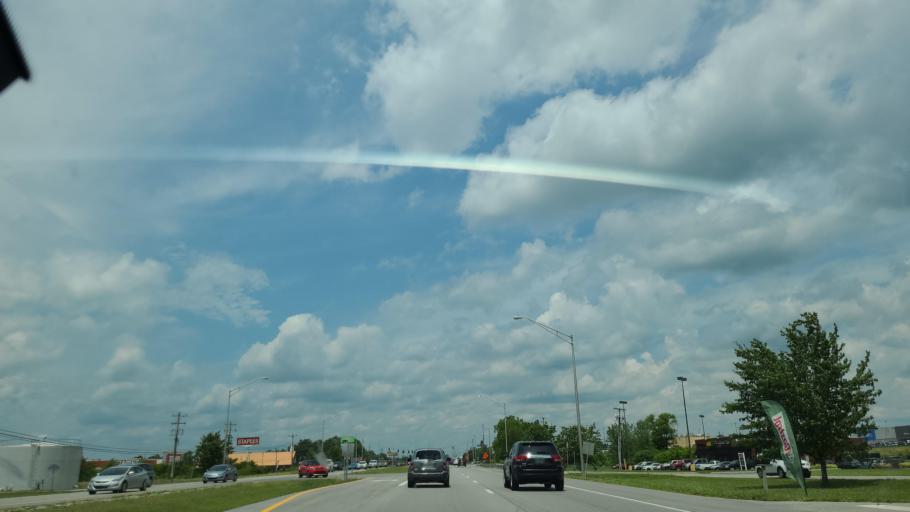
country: US
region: Tennessee
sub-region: Cumberland County
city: Crossville
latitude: 35.9799
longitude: -85.0385
